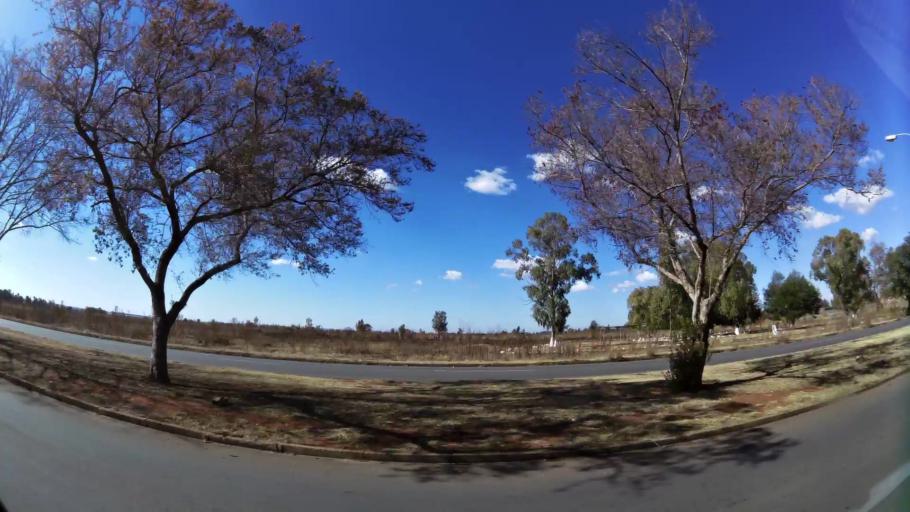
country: ZA
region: Gauteng
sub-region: West Rand District Municipality
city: Carletonville
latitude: -26.3486
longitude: 27.3968
